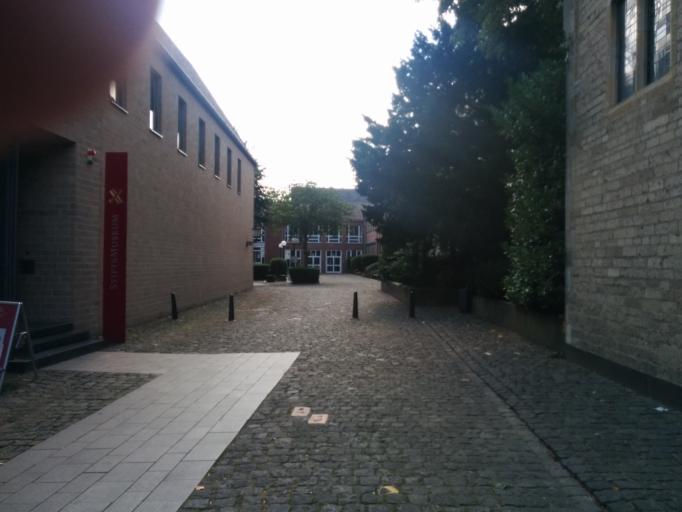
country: DE
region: North Rhine-Westphalia
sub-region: Regierungsbezirk Dusseldorf
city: Xanten
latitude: 51.6628
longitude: 6.4527
